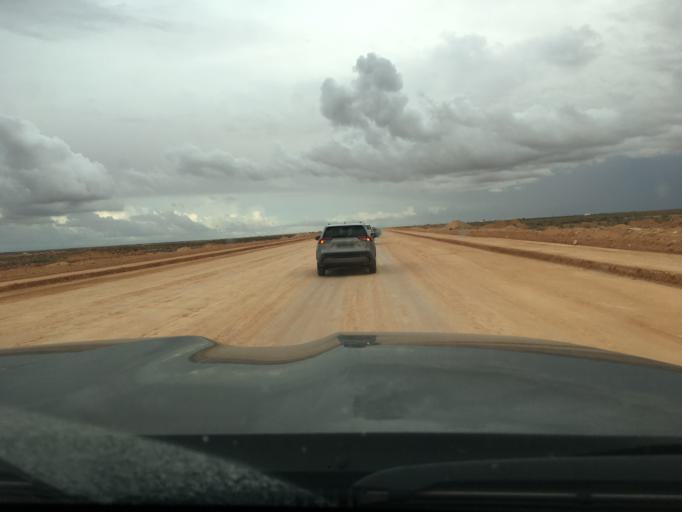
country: TN
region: Madanin
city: Medenine
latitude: 33.2767
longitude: 10.5917
